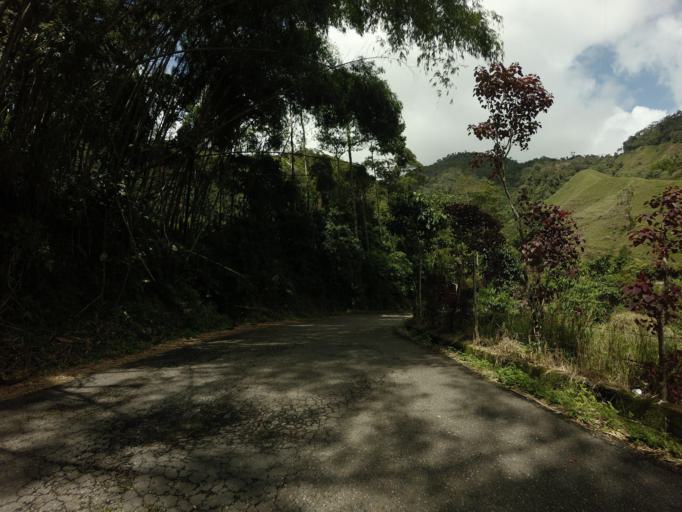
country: CO
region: Caldas
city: Marquetalia
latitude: 5.2747
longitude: -75.1111
